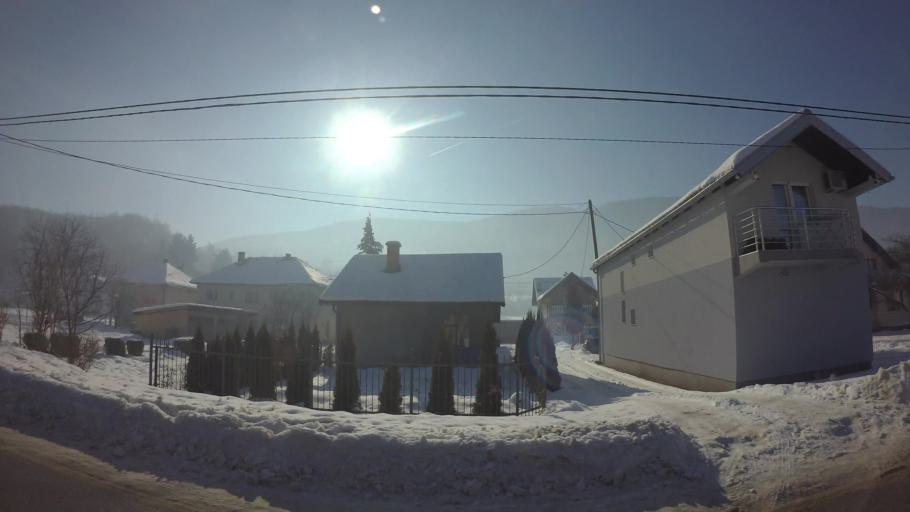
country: BA
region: Federation of Bosnia and Herzegovina
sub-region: Kanton Sarajevo
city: Sarajevo
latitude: 43.7907
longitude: 18.3446
